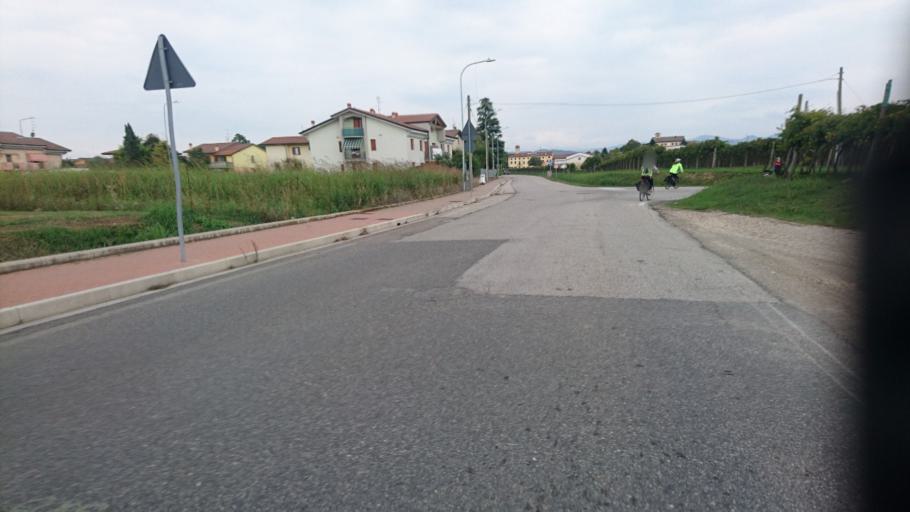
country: IT
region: Veneto
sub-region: Provincia di Verona
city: Caldierino-Rota
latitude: 45.4088
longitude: 11.1516
